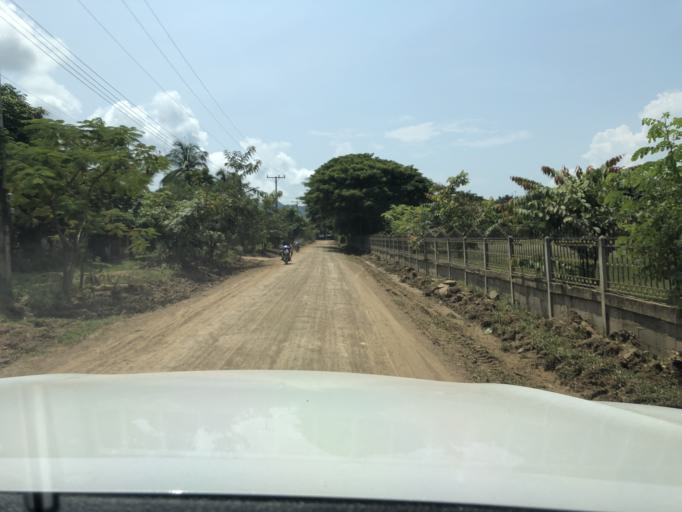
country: LA
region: Xiagnabouli
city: Sainyabuli
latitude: 19.0000
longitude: 101.5112
